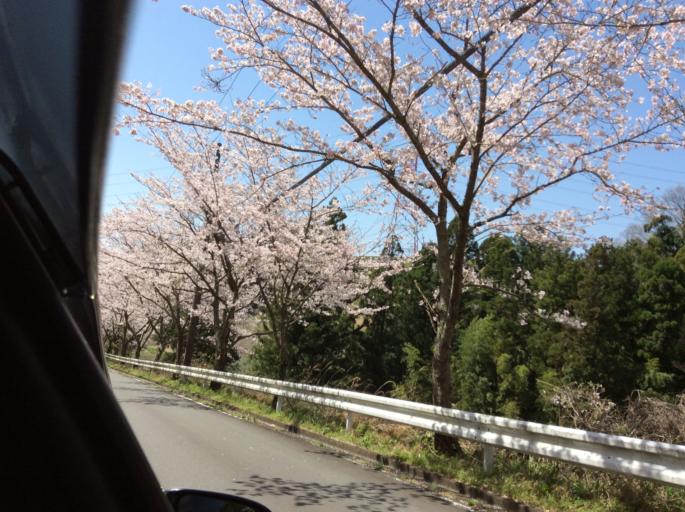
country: JP
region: Shizuoka
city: Kanaya
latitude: 34.7882
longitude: 138.1169
